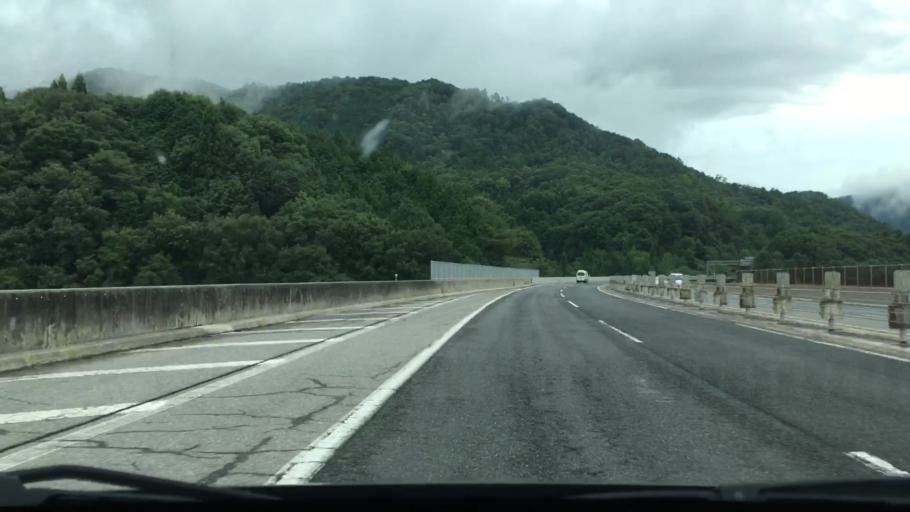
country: JP
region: Hiroshima
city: Hiroshima-shi
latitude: 34.5693
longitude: 132.4563
